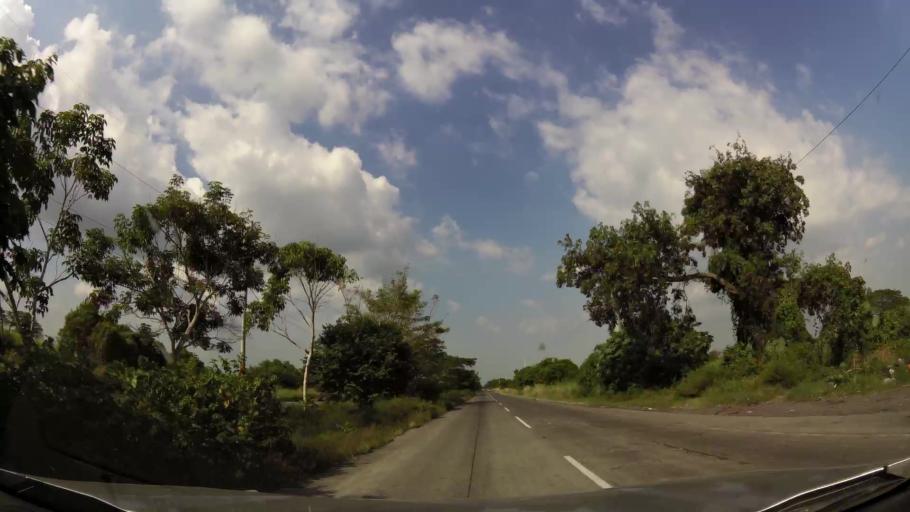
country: GT
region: Escuintla
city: Puerto San Jose
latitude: 14.0303
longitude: -90.7810
